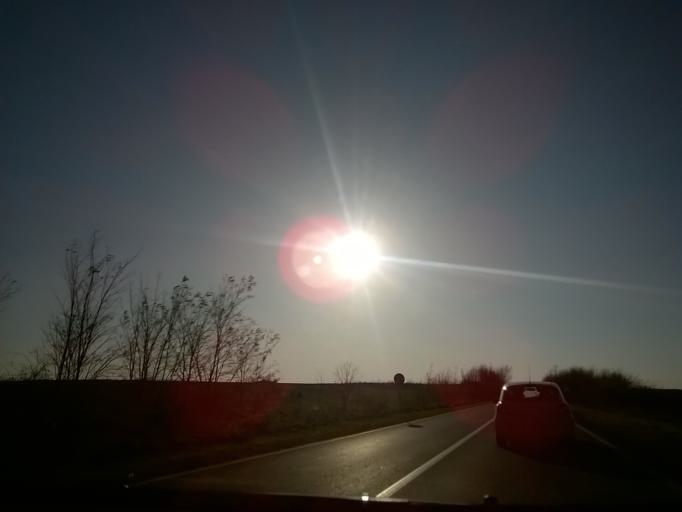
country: RS
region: Autonomna Pokrajina Vojvodina
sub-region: Juznobanatski Okrug
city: Alibunar
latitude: 45.0559
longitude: 20.9166
